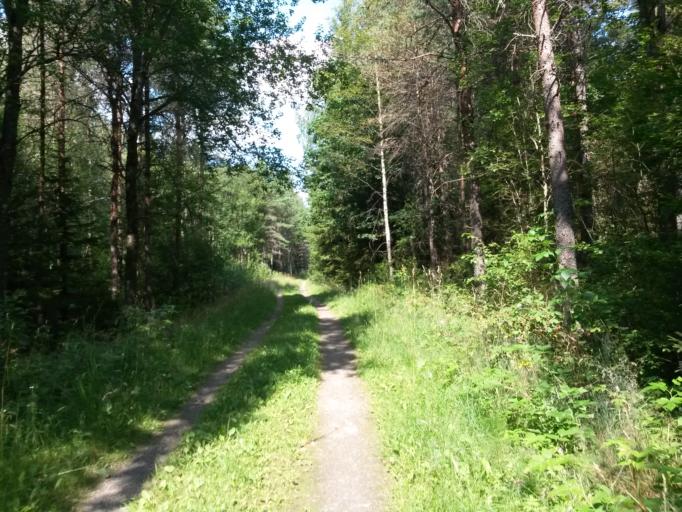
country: SE
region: Vaestra Goetaland
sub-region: Vargarda Kommun
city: Vargarda
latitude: 58.0372
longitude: 12.8296
